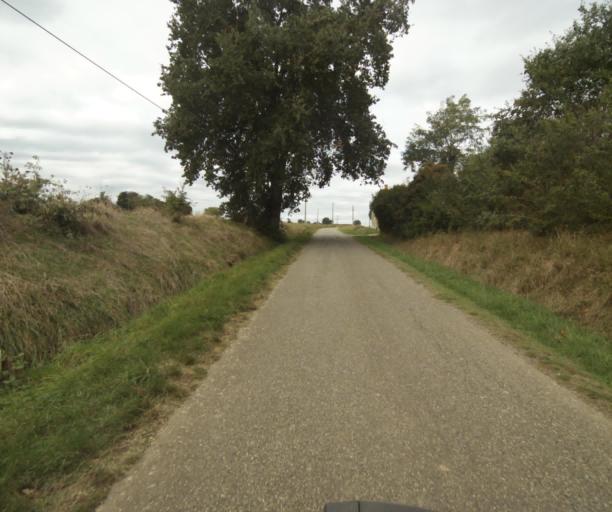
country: FR
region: Midi-Pyrenees
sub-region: Departement du Tarn-et-Garonne
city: Verdun-sur-Garonne
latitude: 43.8674
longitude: 1.1705
